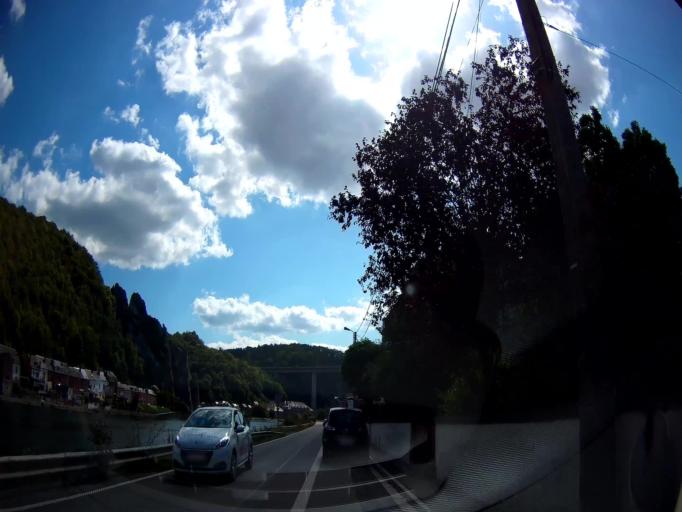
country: BE
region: Wallonia
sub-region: Province de Namur
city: Dinant
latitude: 50.2469
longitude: 4.9190
